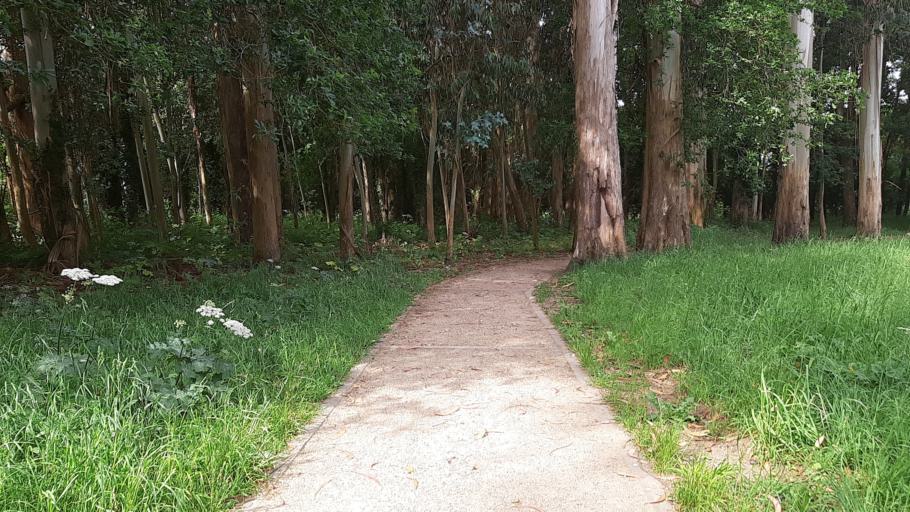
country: ES
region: Galicia
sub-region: Provincia de Pontevedra
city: O Rosal
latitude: 41.9212
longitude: -8.8261
